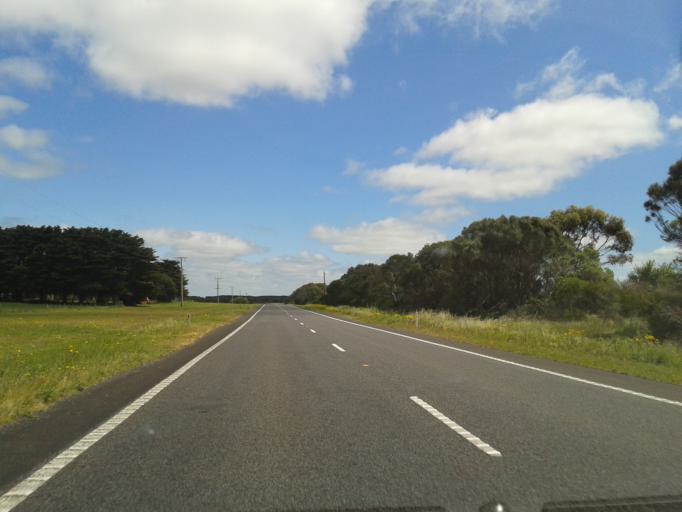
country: AU
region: Victoria
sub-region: Moyne
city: Port Fairy
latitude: -38.3042
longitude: 142.0355
